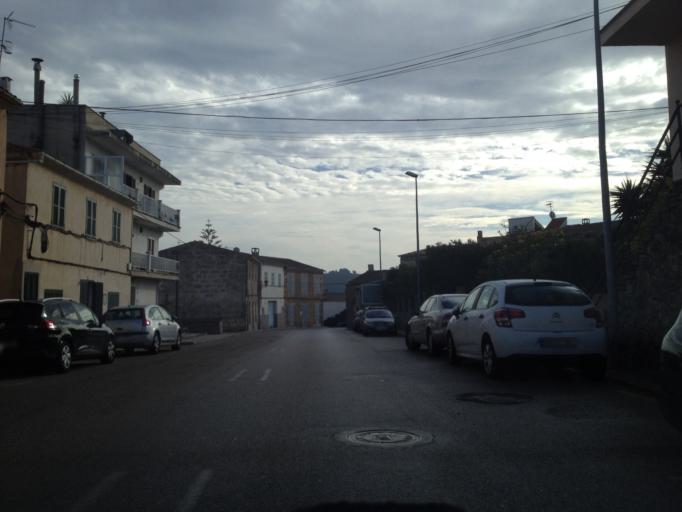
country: ES
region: Balearic Islands
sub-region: Illes Balears
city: Son Servera
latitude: 39.6254
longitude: 3.3544
